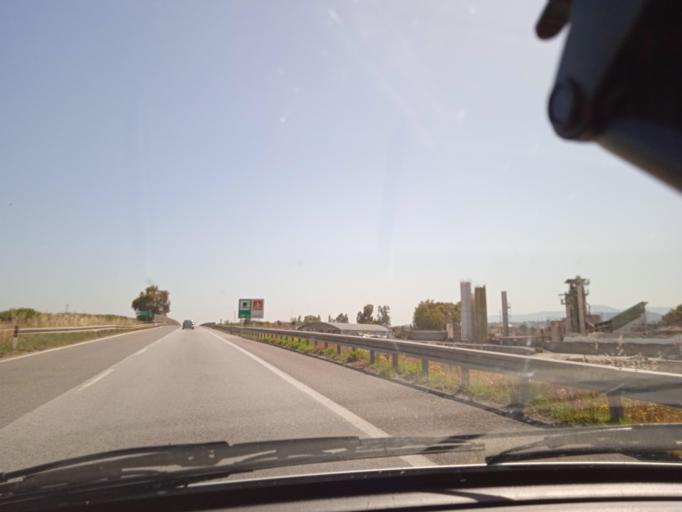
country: IT
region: Sicily
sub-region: Messina
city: Meri
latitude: 38.1729
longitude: 15.2344
